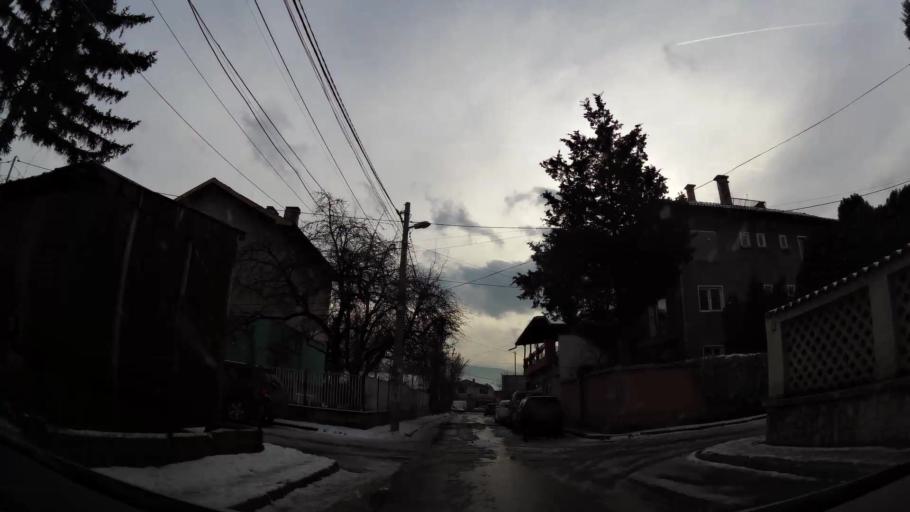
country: BG
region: Sofia-Capital
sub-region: Stolichna Obshtina
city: Sofia
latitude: 42.7227
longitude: 23.3312
